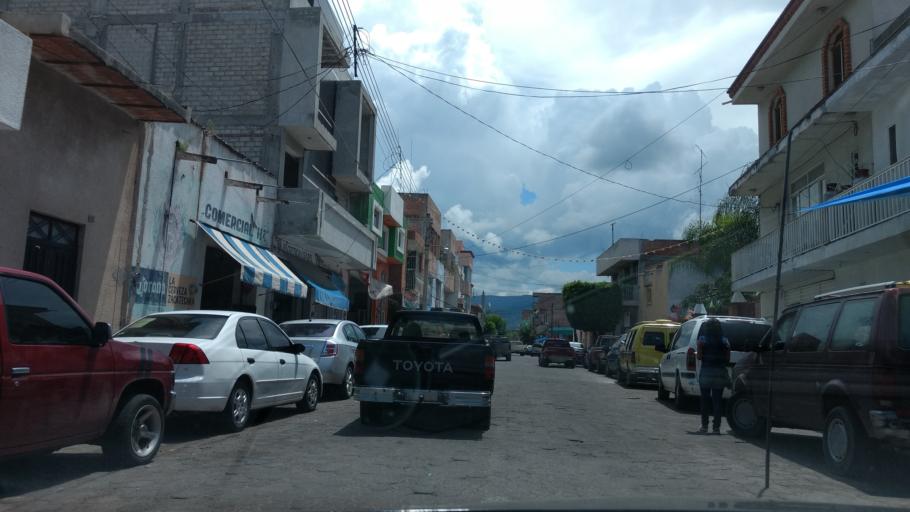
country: MX
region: Zacatecas
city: Tlaltenango de Sanchez Roman
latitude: 21.7823
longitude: -103.3029
